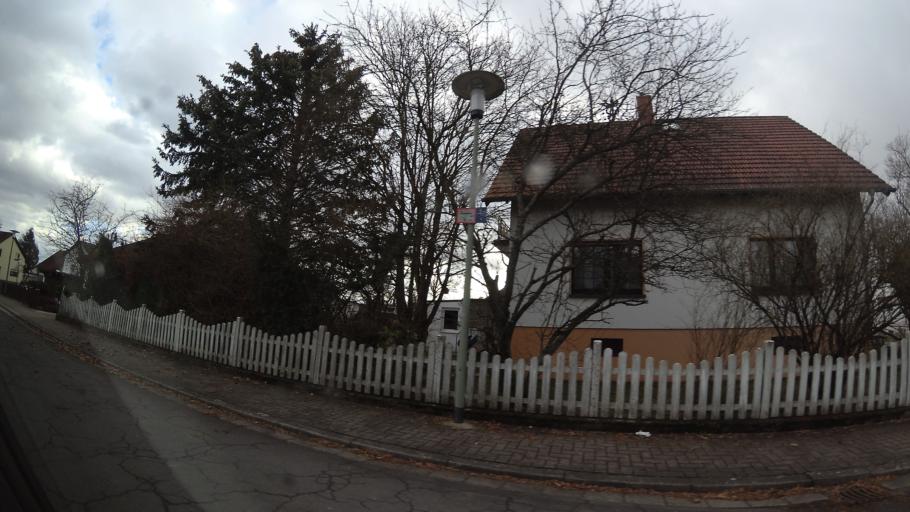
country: DE
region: Saarland
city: Bexbach
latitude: 49.3654
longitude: 7.2734
